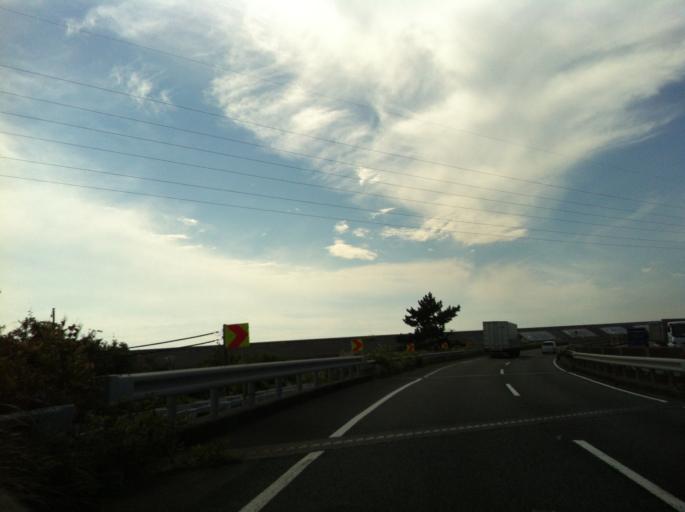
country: JP
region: Shizuoka
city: Fuji
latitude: 35.1171
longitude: 138.6230
